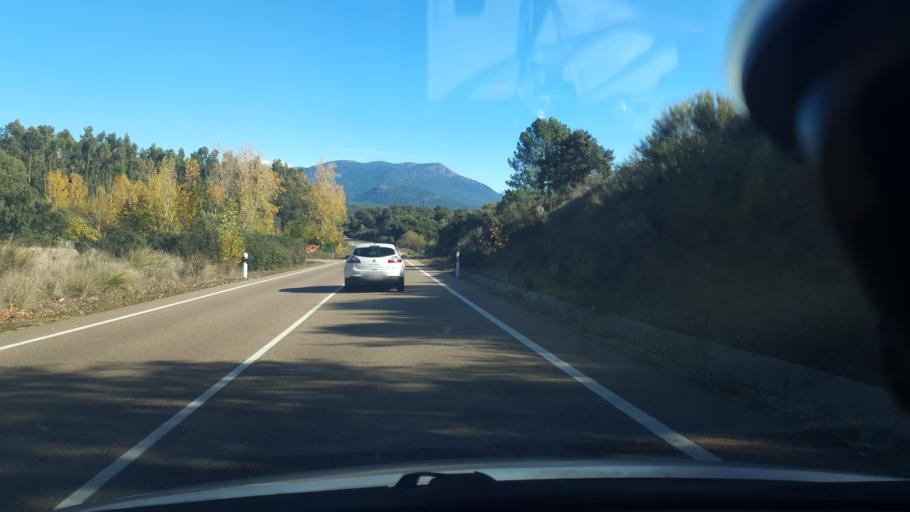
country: ES
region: Castille and Leon
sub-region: Provincia de Avila
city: Arenas de San Pedro
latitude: 40.1641
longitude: -5.1077
